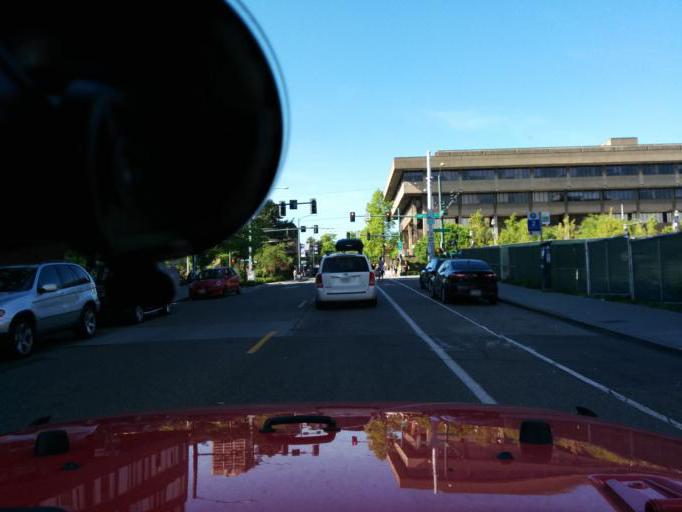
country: US
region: Washington
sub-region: King County
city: Seattle
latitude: 47.6555
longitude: -122.3133
